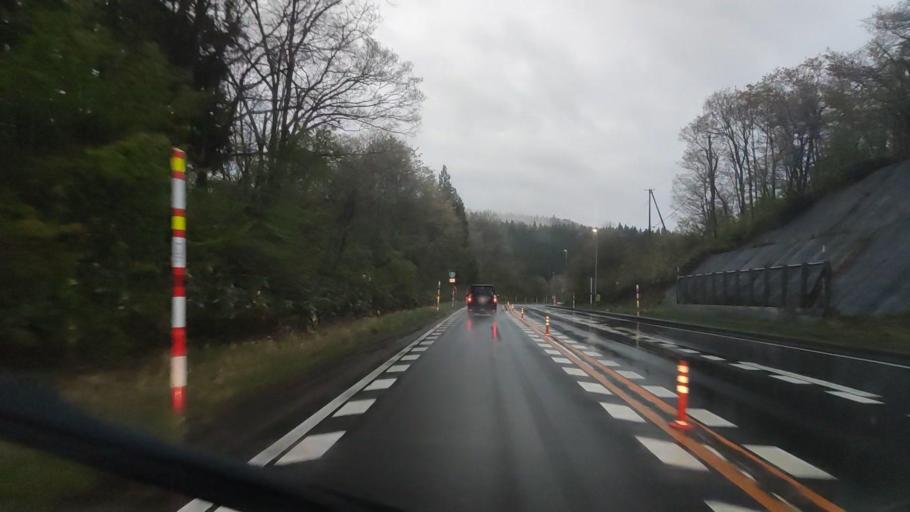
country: JP
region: Akita
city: Omagari
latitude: 39.5766
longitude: 140.3258
